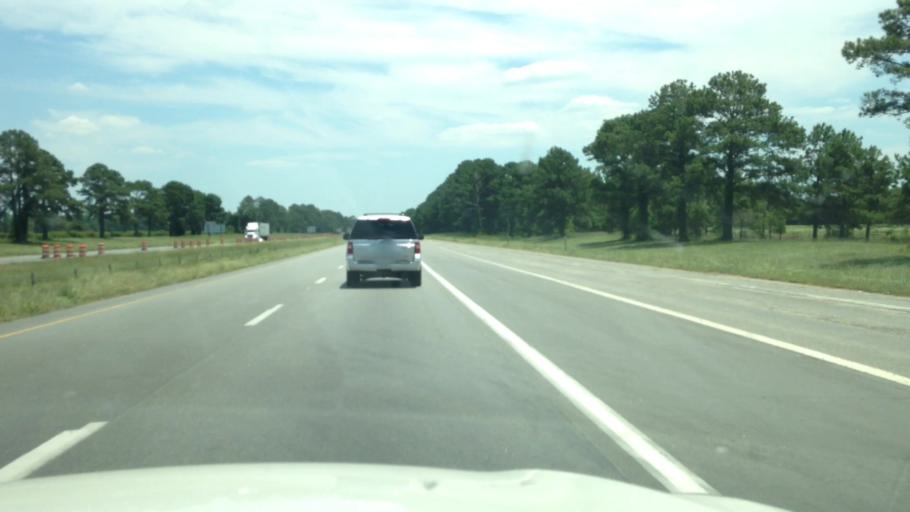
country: US
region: South Carolina
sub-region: Lee County
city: Bishopville
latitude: 34.1936
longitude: -80.2757
